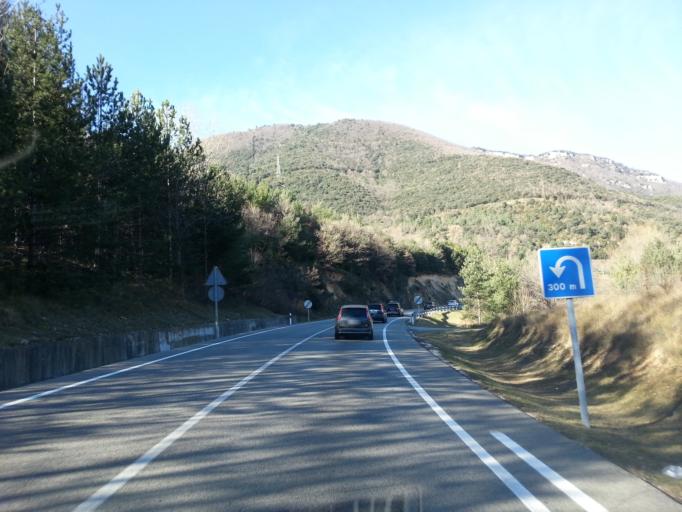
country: ES
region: Catalonia
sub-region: Provincia de Barcelona
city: Berga
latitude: 42.1523
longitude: 1.8598
